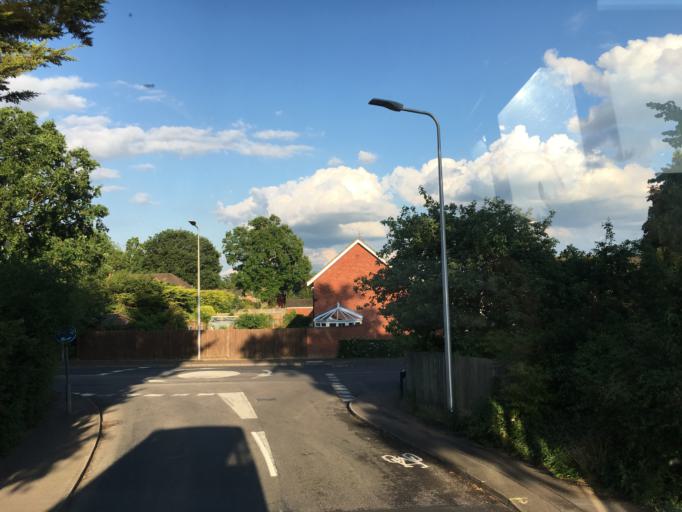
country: GB
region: England
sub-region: West Berkshire
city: Calcot
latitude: 51.4414
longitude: -1.0336
